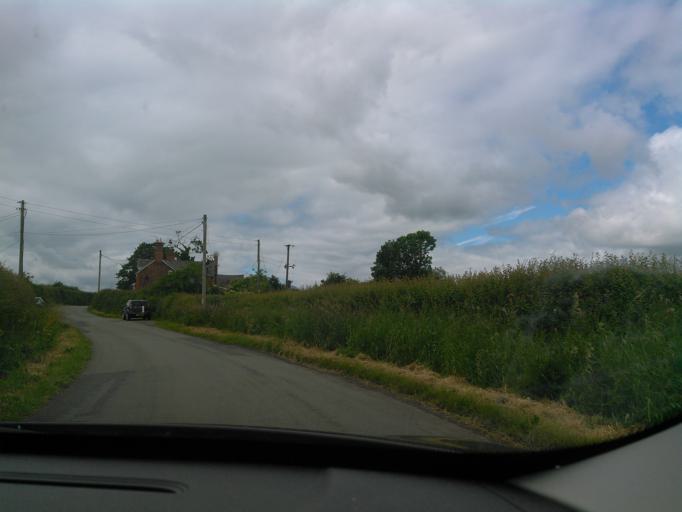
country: GB
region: England
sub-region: Shropshire
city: Wem
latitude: 52.9110
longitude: -2.7408
